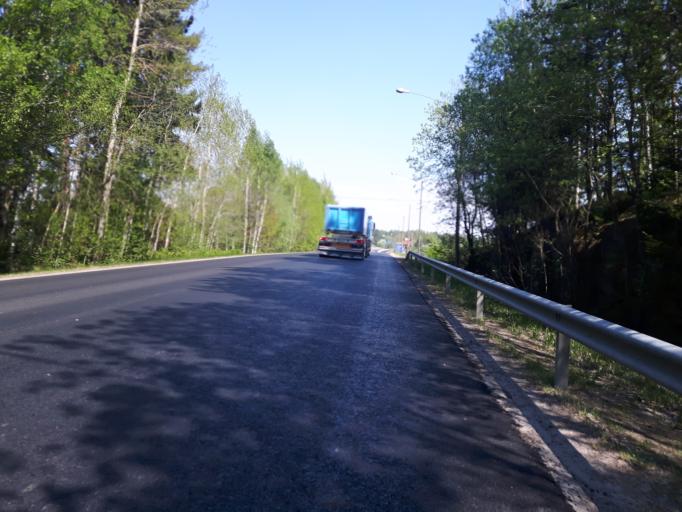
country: FI
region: Uusimaa
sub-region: Helsinki
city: Pornainen
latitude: 60.3376
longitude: 25.4648
